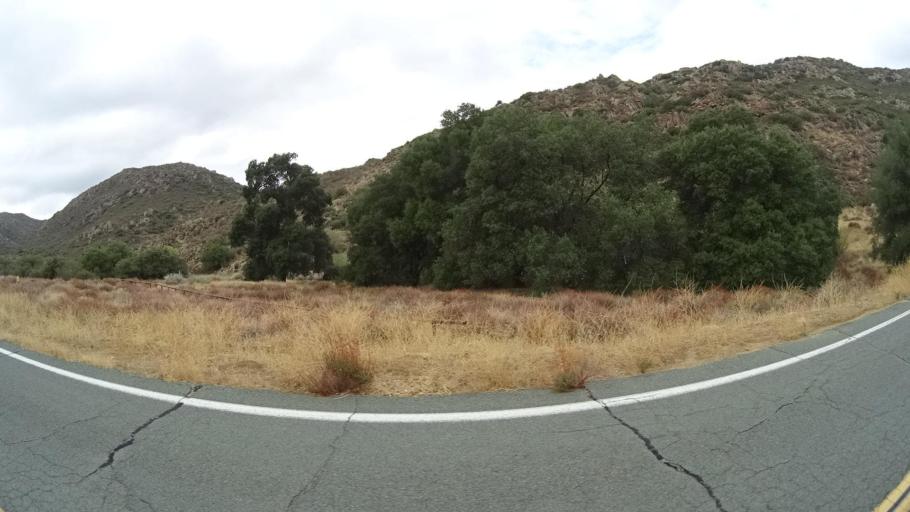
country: US
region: California
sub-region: San Diego County
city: Pine Valley
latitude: 32.7516
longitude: -116.4520
